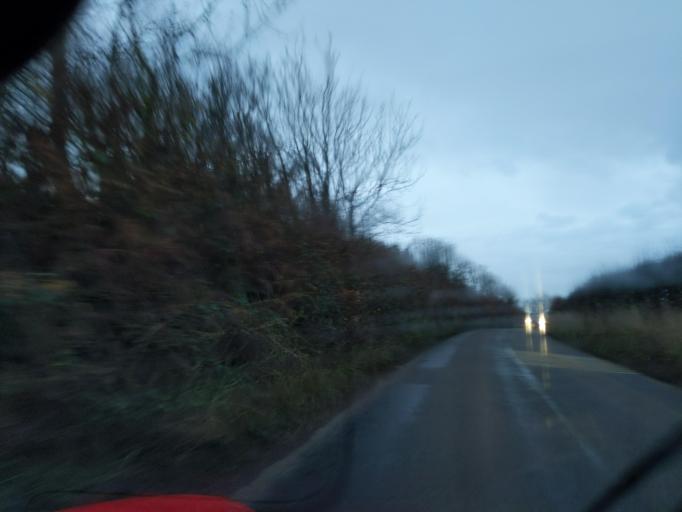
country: GB
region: England
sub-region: Devon
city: Wembury
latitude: 50.3352
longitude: -4.0699
